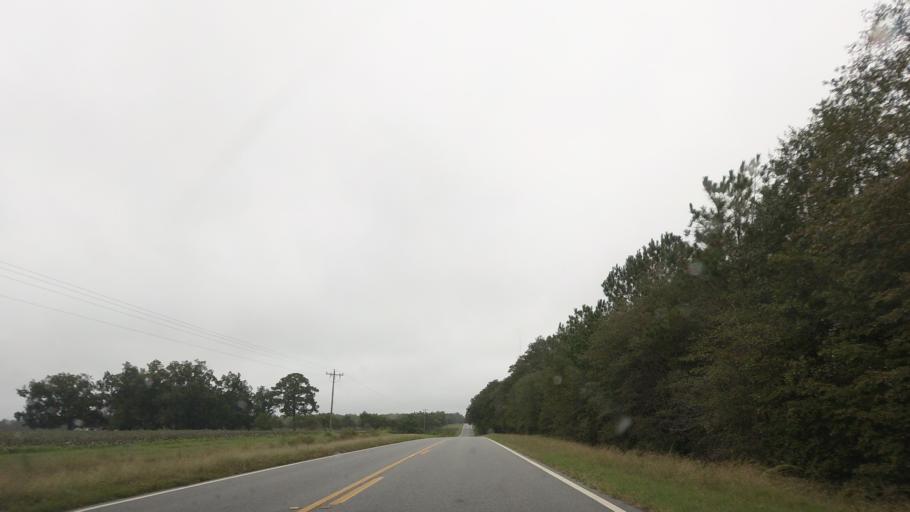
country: US
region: Georgia
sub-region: Berrien County
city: Enigma
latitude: 31.4621
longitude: -83.2383
